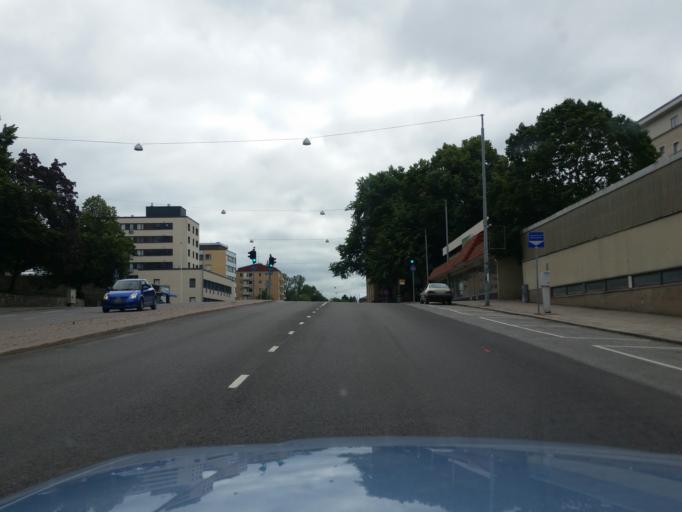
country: FI
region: Varsinais-Suomi
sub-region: Turku
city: Turku
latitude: 60.4488
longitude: 22.2801
